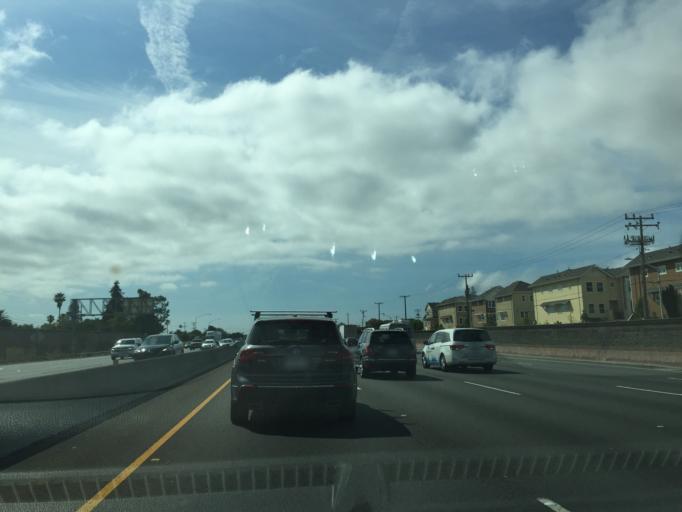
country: US
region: California
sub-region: San Mateo County
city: San Mateo
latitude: 37.5660
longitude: -122.3087
